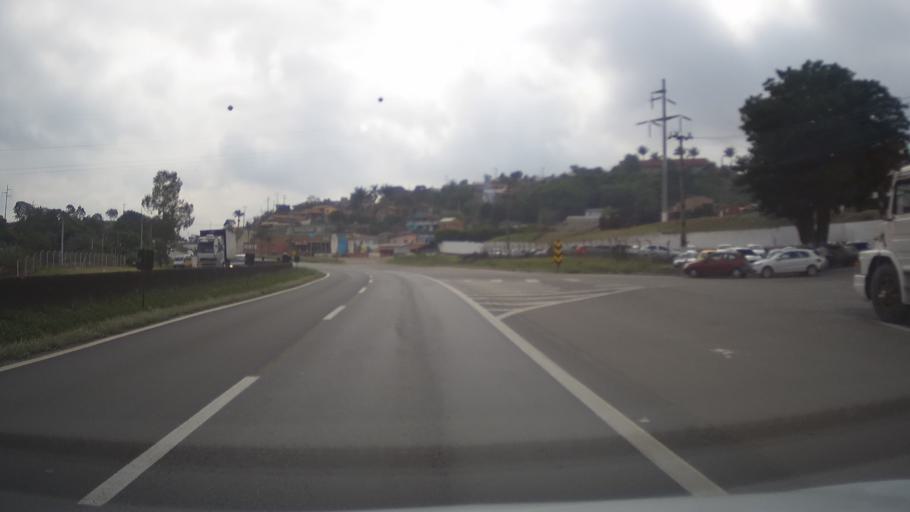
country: BR
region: Minas Gerais
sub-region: Extrema
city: Extrema
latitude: -22.8252
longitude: -46.3111
